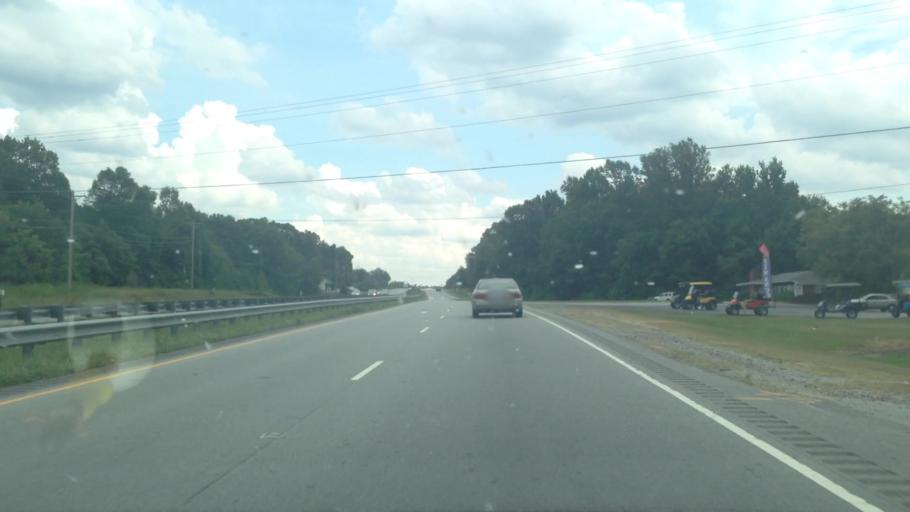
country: US
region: North Carolina
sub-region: Rockingham County
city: Madison
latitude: 36.3527
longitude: -79.9464
